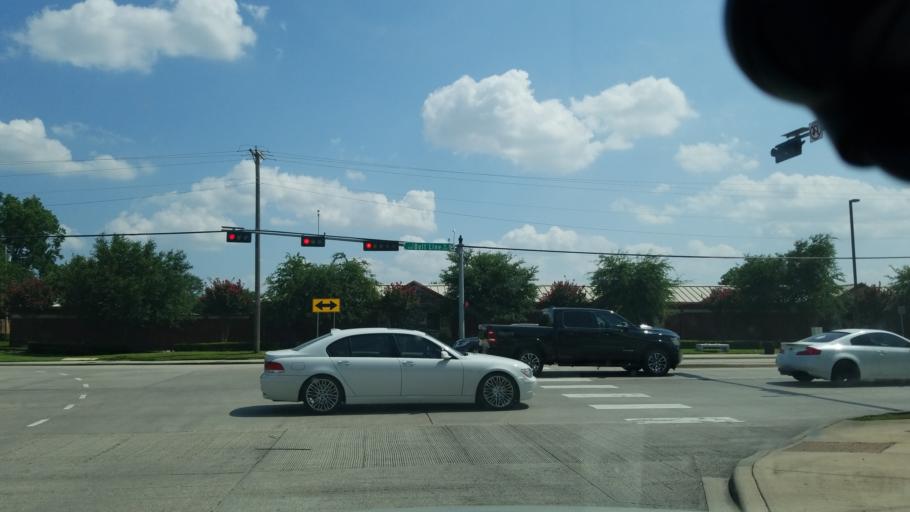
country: US
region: Texas
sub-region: Dallas County
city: Carrollton
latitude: 32.9538
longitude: -96.8775
